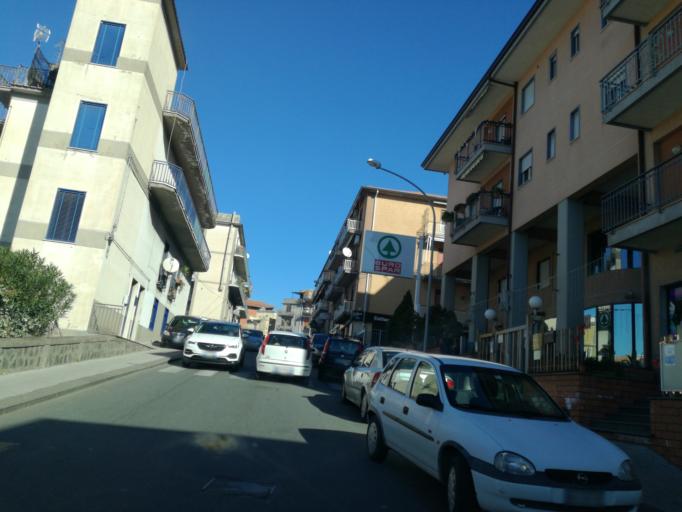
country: IT
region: Sicily
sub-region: Catania
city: Bronte
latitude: 37.7847
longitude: 14.8374
